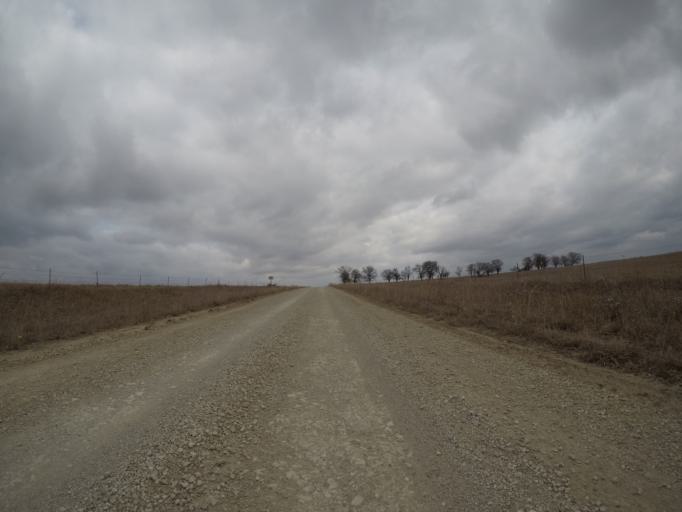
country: US
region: Kansas
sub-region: Morris County
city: Council Grove
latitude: 38.7369
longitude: -96.2796
